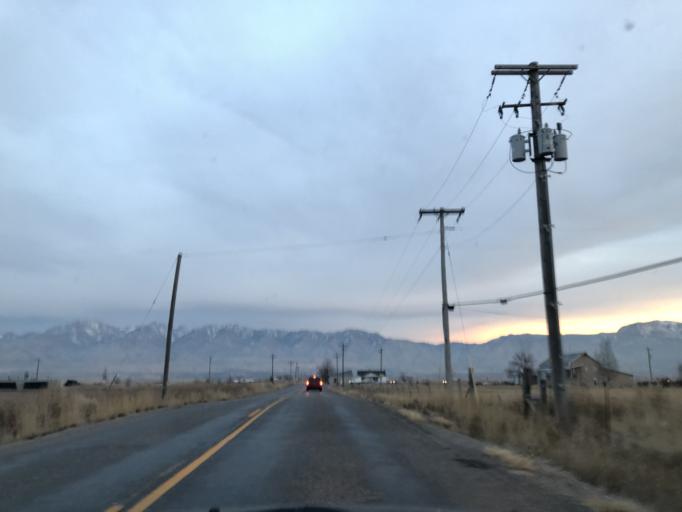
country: US
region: Utah
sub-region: Cache County
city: Benson
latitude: 41.7947
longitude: -111.8942
